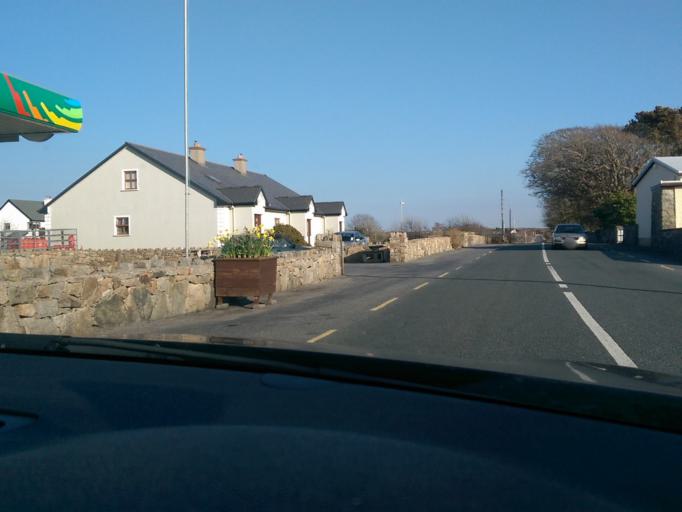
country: IE
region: Connaught
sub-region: County Galway
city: Clifden
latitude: 53.3245
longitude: -9.8182
